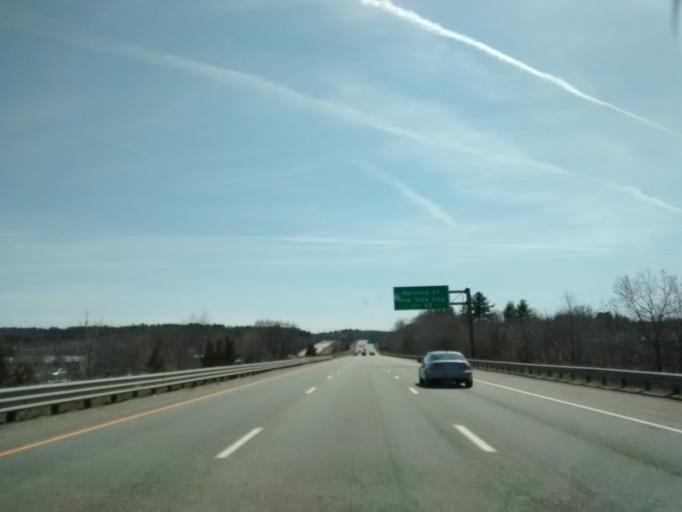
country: US
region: Massachusetts
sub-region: Worcester County
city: Cordaville
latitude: 42.2757
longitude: -71.5662
